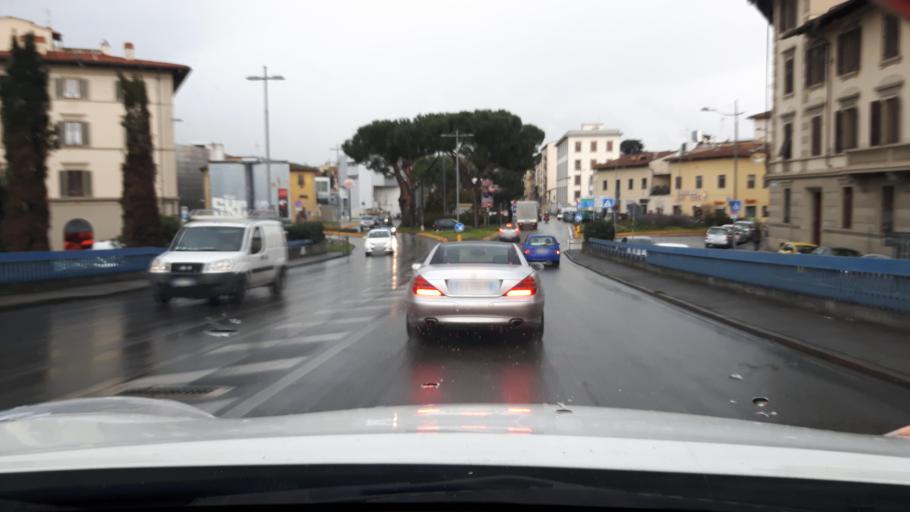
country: IT
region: Tuscany
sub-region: Province of Florence
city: Fiesole
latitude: 43.7707
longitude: 11.2823
